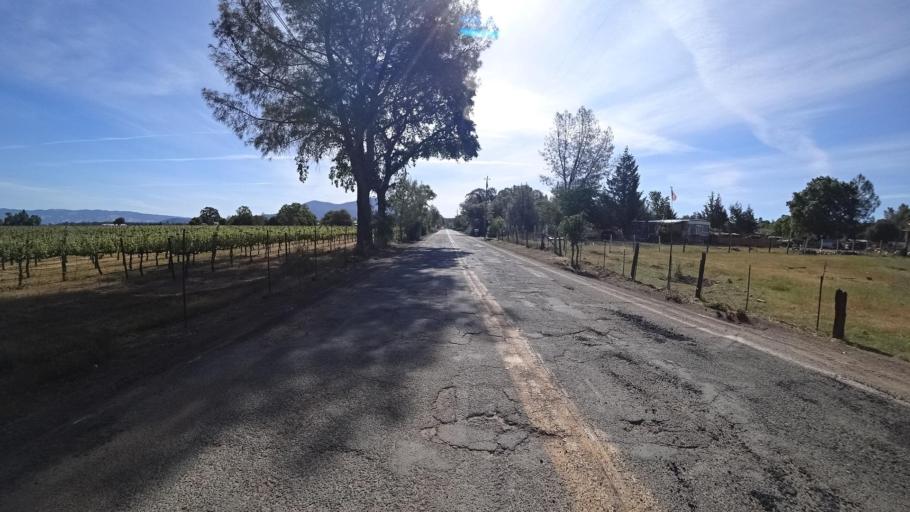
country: US
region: California
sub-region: Lake County
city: Kelseyville
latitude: 38.9574
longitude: -122.8904
